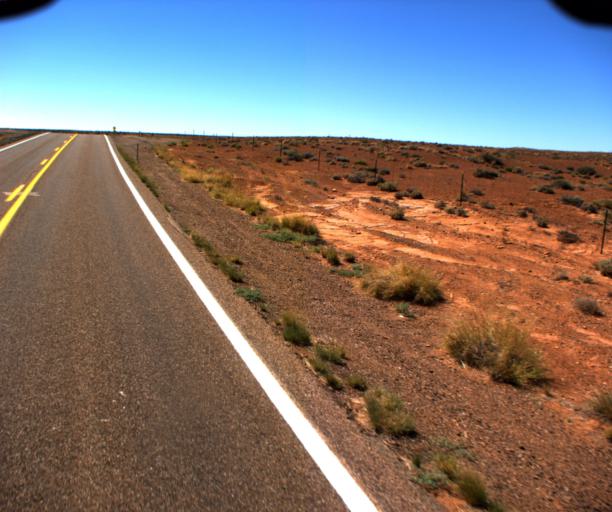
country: US
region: Arizona
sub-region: Navajo County
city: Winslow
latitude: 34.9735
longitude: -110.6503
